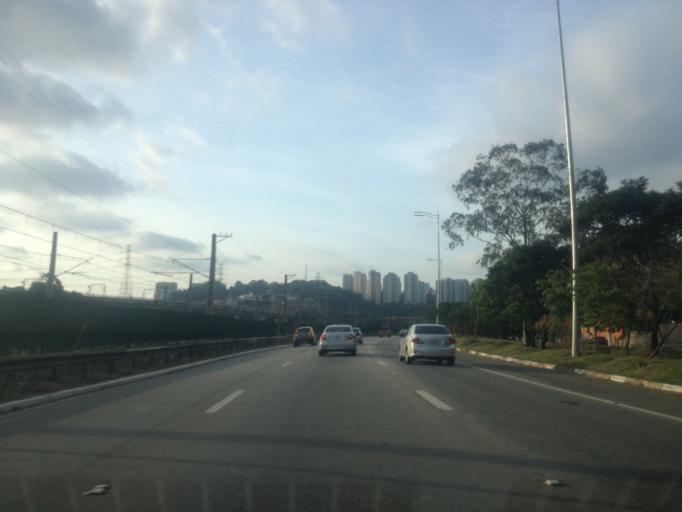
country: BR
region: Sao Paulo
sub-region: Taboao Da Serra
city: Taboao da Serra
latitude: -23.6499
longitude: -46.7244
